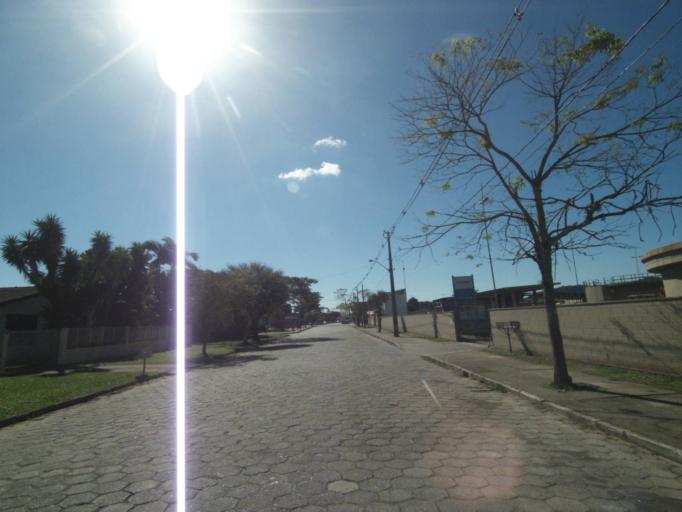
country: BR
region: Parana
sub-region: Paranagua
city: Paranagua
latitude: -25.5130
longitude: -48.5032
